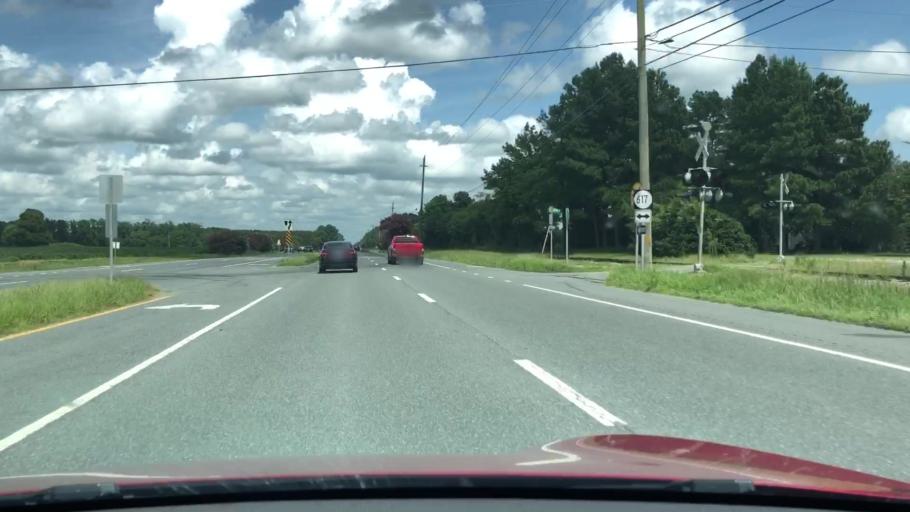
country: US
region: Virginia
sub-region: Northampton County
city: Exmore
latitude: 37.4576
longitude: -75.8700
